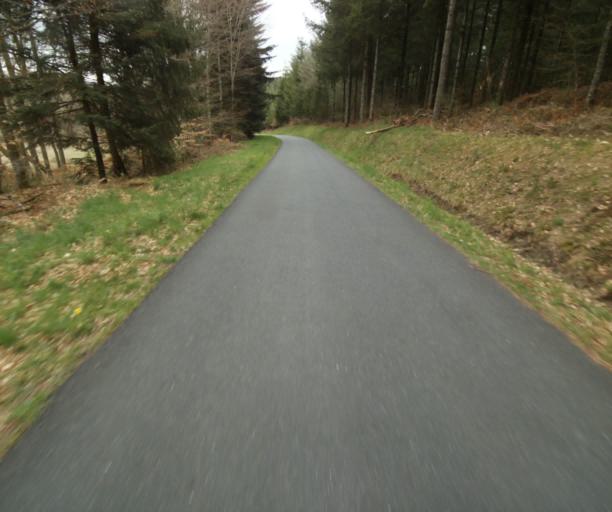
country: FR
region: Limousin
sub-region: Departement de la Correze
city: Correze
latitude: 45.3077
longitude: 1.9039
